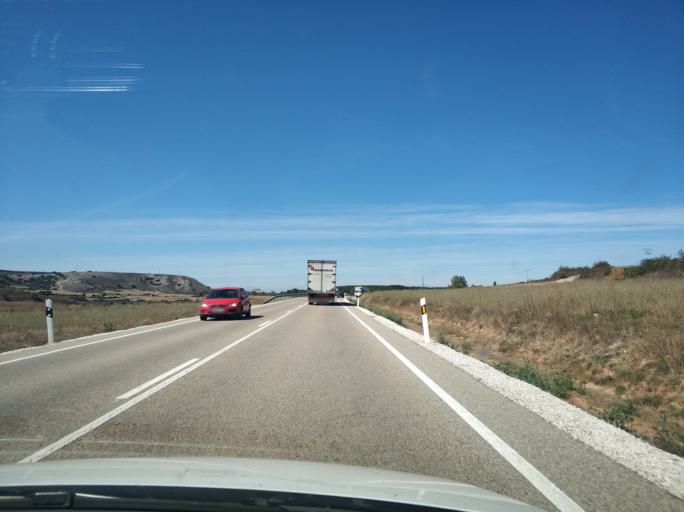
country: ES
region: Castille and Leon
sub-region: Provincia de Burgos
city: Montorio
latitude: 42.6105
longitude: -3.8114
